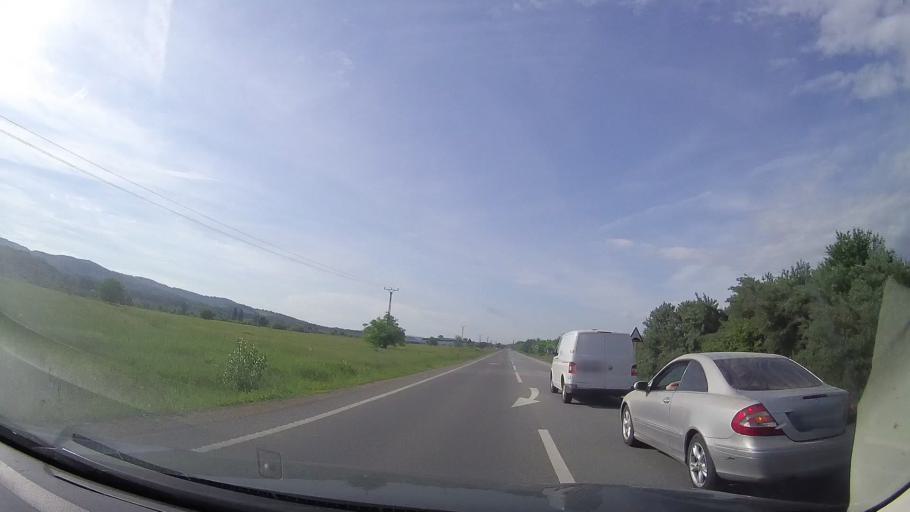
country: RO
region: Caras-Severin
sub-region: Comuna Buchin
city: Buchin
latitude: 45.3753
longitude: 22.2360
